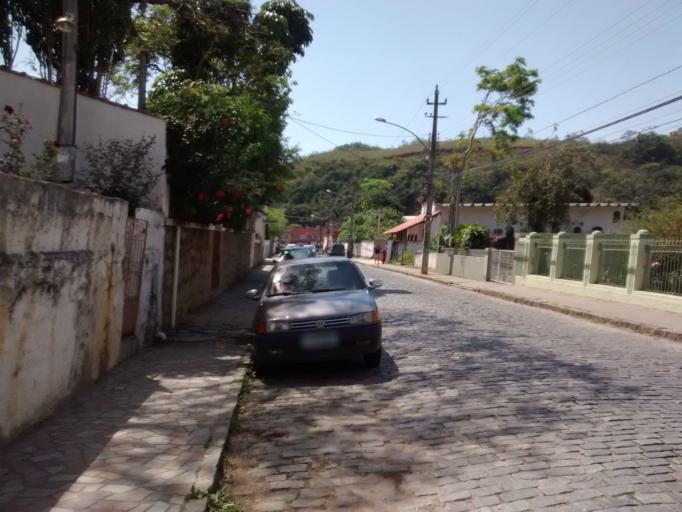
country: BR
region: Rio de Janeiro
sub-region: Miguel Pereira
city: Miguel Pereira
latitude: -22.4563
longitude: -43.4694
